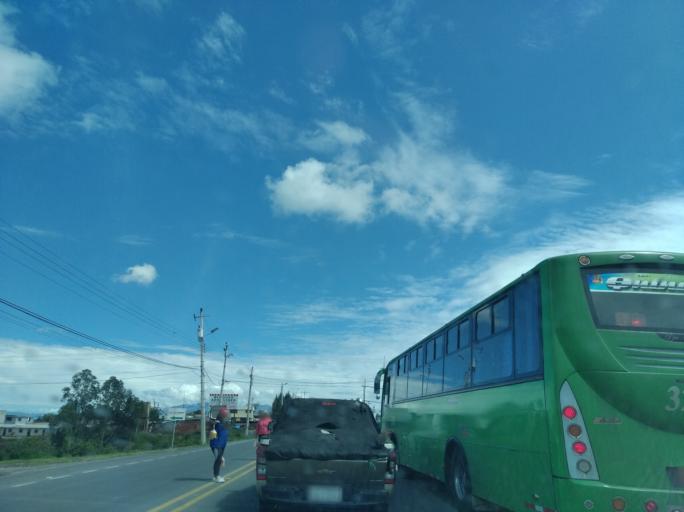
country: EC
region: Pichincha
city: Sangolqui
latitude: -0.1776
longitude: -78.3290
